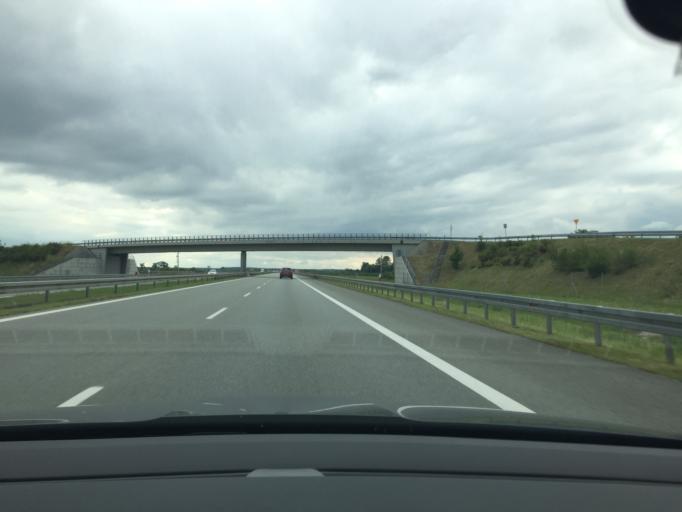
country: PL
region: Greater Poland Voivodeship
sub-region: Powiat nowotomyski
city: Kuslin
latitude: 52.3825
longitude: 16.3659
